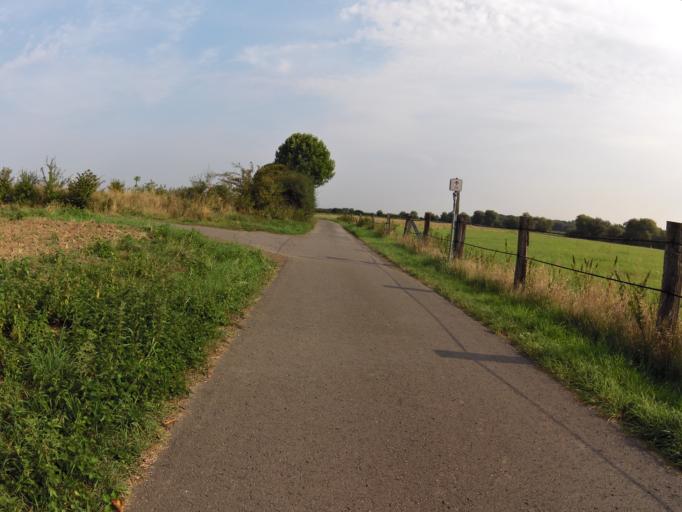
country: DE
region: Lower Saxony
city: Raddestorf
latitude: 52.4576
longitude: 9.0168
